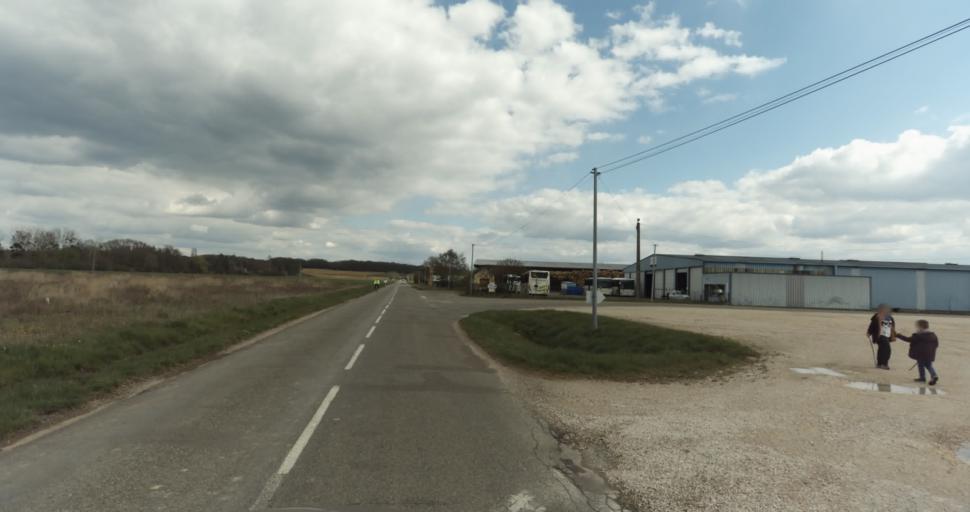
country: FR
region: Bourgogne
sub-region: Departement de la Cote-d'Or
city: Auxonne
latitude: 47.1961
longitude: 5.4169
